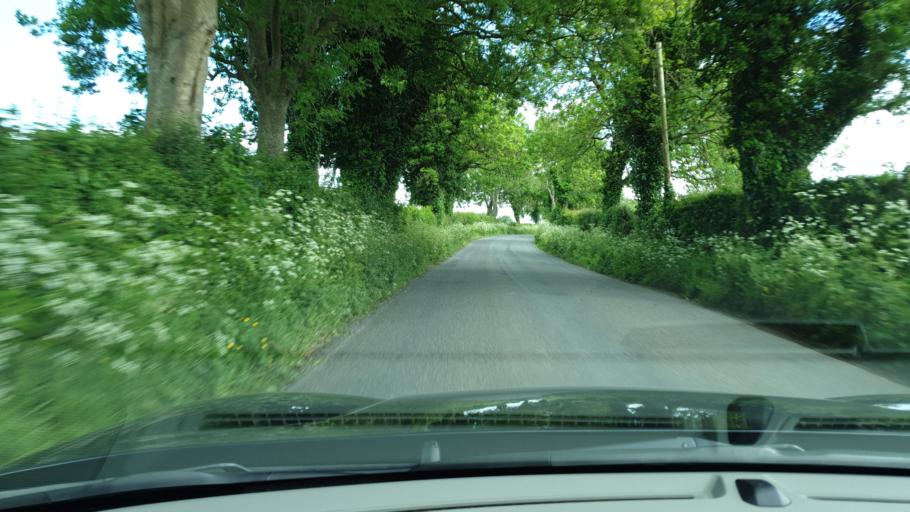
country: IE
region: Leinster
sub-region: An Mhi
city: Navan
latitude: 53.7937
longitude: -6.6877
